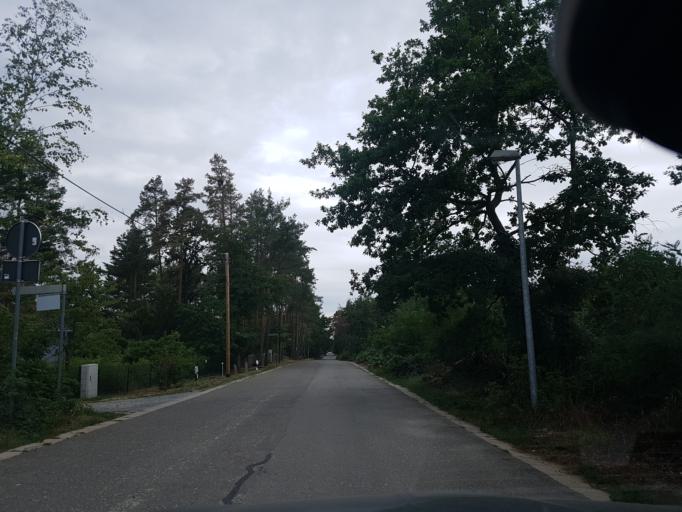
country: DE
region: Brandenburg
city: Bad Liebenwerda
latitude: 51.5047
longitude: 13.4377
